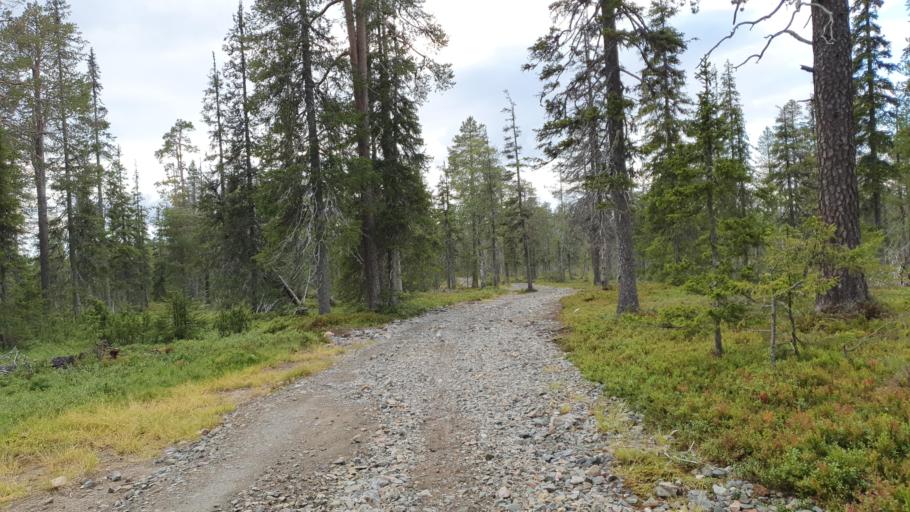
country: FI
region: Lapland
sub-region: Tunturi-Lappi
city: Kolari
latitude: 67.6183
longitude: 24.2325
